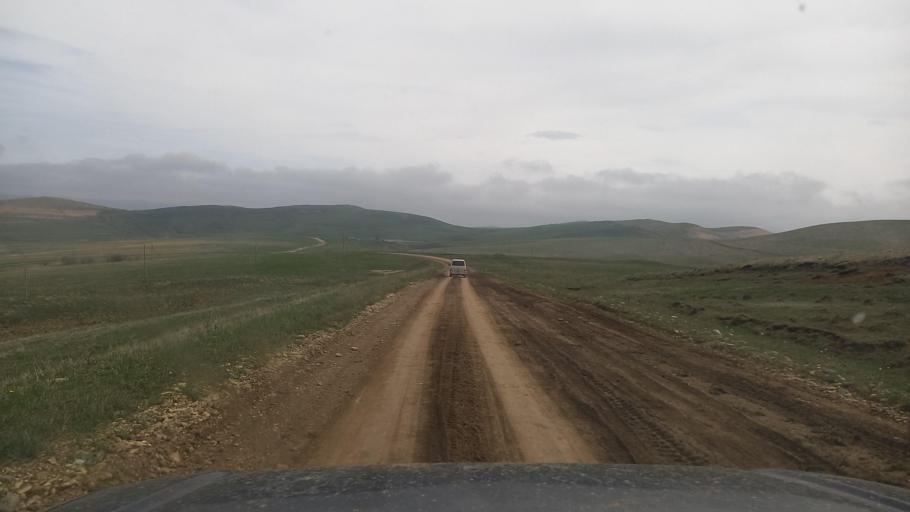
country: RU
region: Stavropol'skiy
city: Kislovodsk
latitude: 43.7691
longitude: 42.8361
